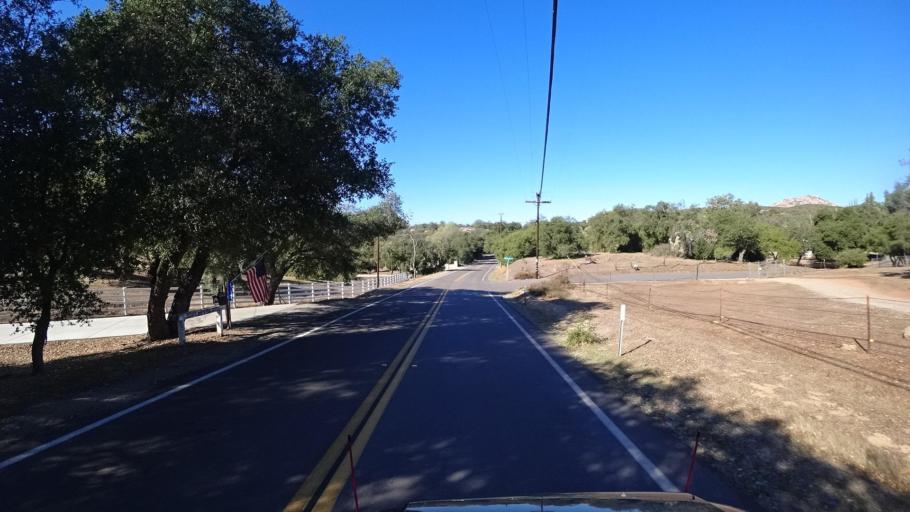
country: MX
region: Baja California
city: Tecate
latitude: 32.6762
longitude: -116.7283
